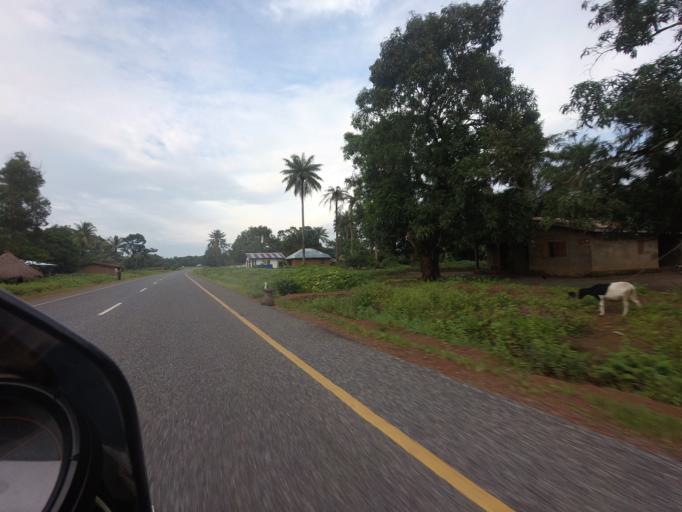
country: SL
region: Northern Province
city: Kambia
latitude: 9.0304
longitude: -12.9371
